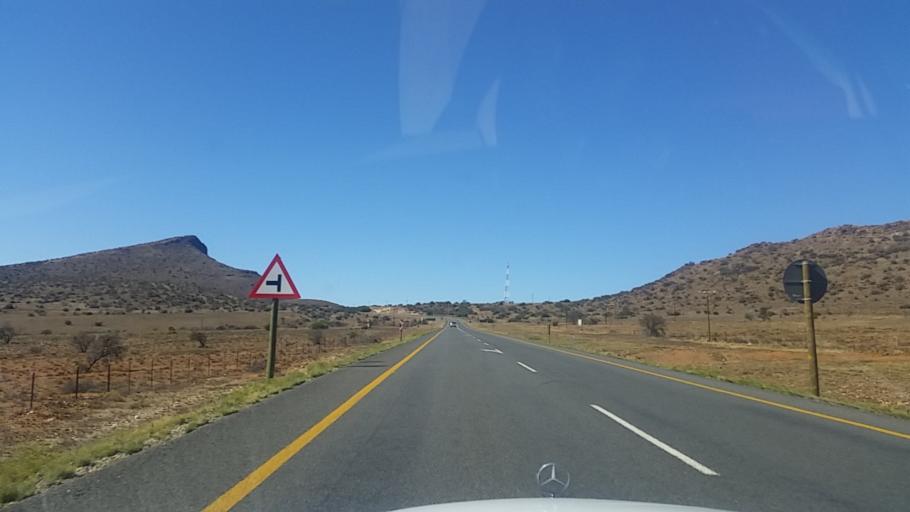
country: ZA
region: Eastern Cape
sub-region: Cacadu District Municipality
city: Graaff-Reinet
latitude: -32.1013
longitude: 24.6055
